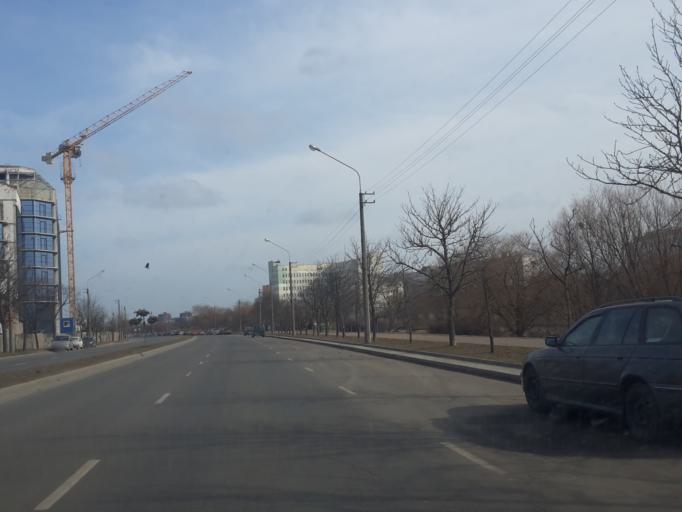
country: BY
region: Minsk
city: Minsk
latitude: 53.9031
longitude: 27.6046
